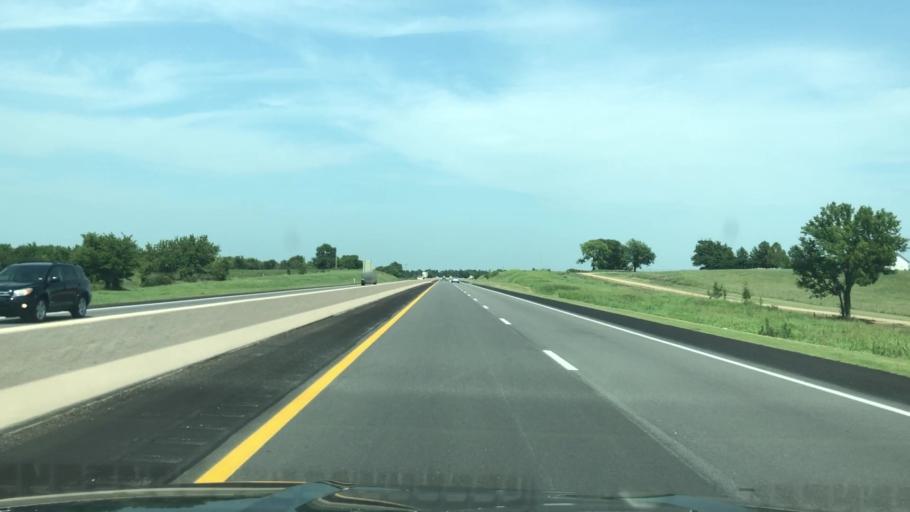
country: US
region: Oklahoma
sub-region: Craig County
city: Vinita
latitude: 36.6504
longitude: -95.1088
